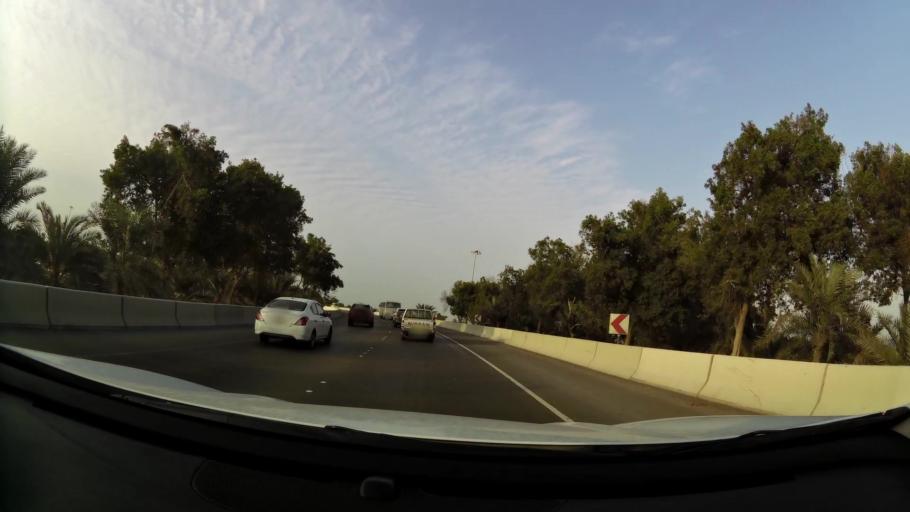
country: AE
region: Abu Dhabi
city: Abu Dhabi
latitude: 24.3909
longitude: 54.5267
